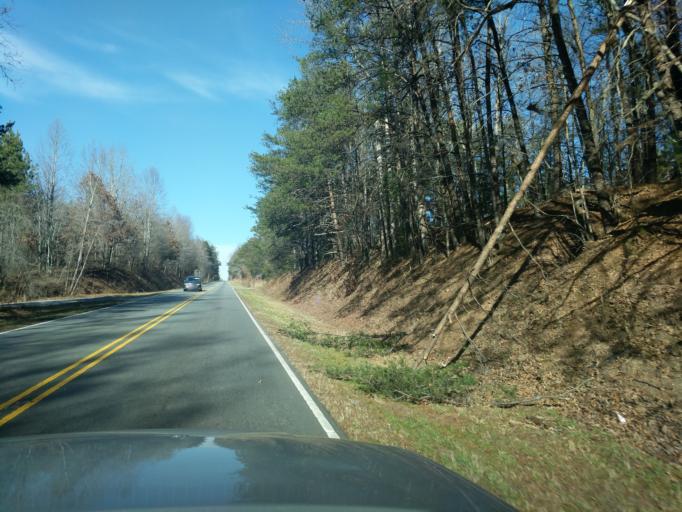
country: US
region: North Carolina
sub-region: Rutherford County
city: Rutherfordton
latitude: 35.4613
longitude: -81.9794
